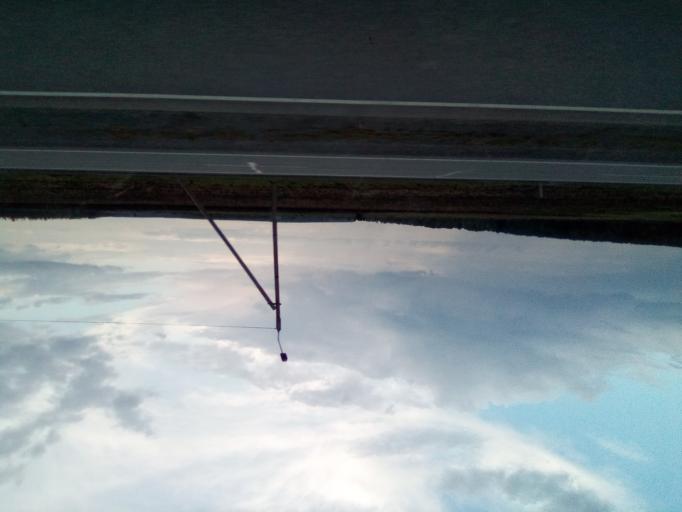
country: RU
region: Chelyabinsk
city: Poletayevo
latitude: 54.9901
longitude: 61.0502
